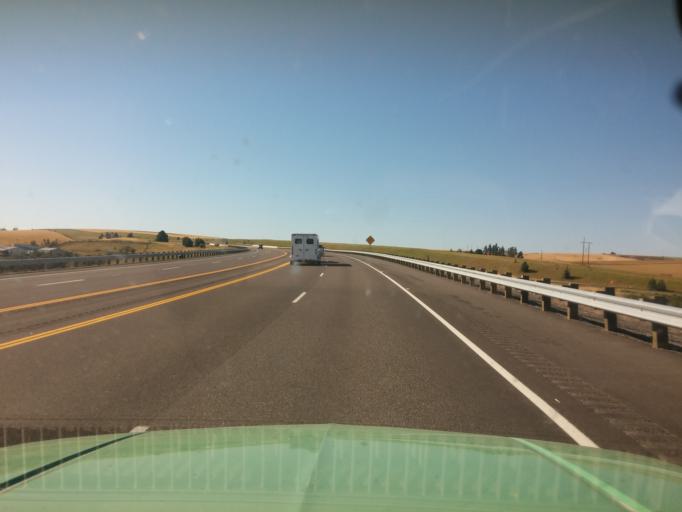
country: US
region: Washington
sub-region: Asotin County
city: Clarkston
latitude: 46.4772
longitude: -117.0385
